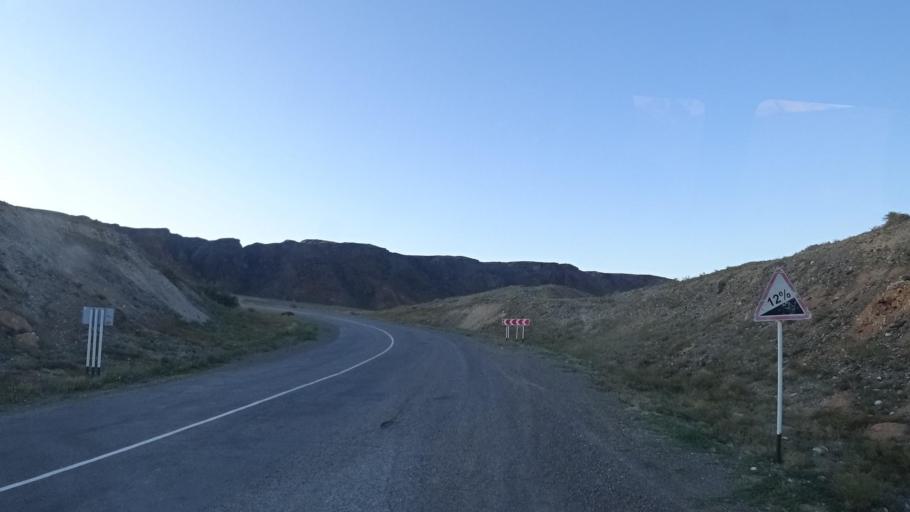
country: KZ
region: Almaty Oblysy
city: Kegen
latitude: 43.2701
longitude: 78.9726
